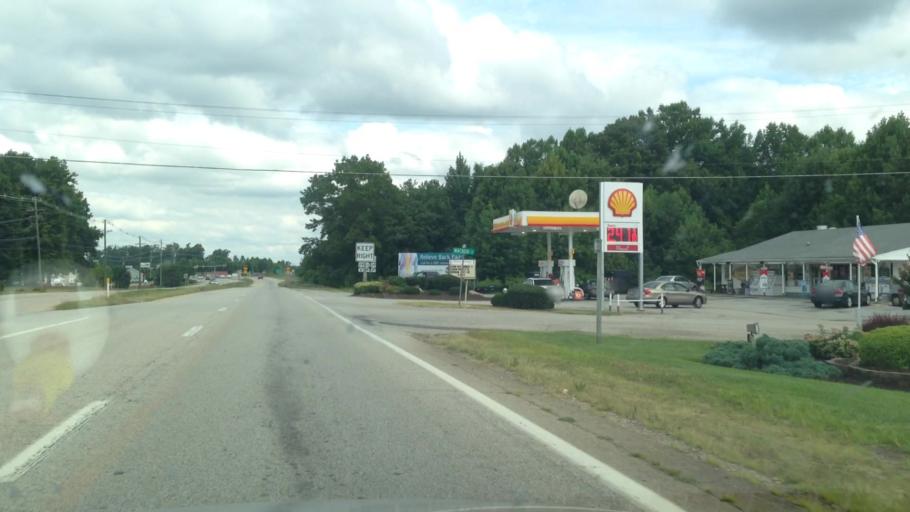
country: US
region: Virginia
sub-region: Pittsylvania County
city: Mount Hermon
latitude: 36.6923
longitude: -79.3670
